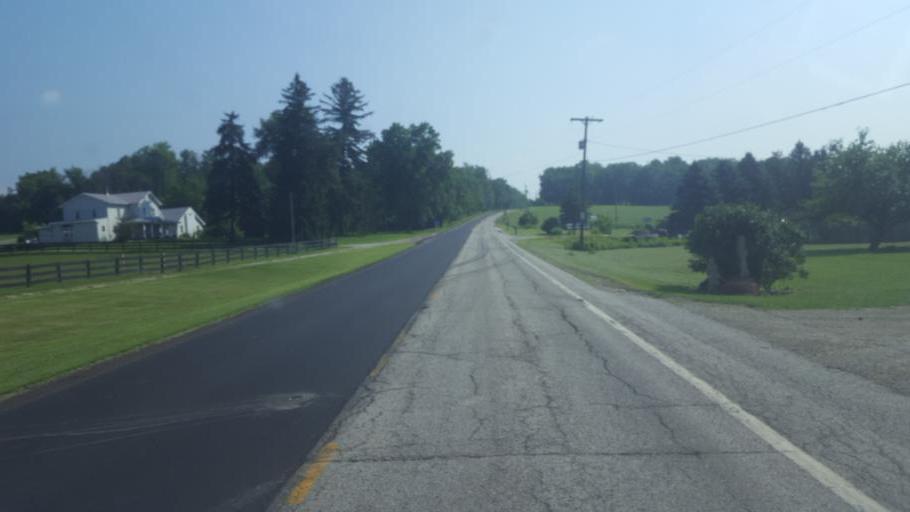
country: US
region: Ohio
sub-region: Richland County
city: Lexington
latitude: 40.6322
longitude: -82.6459
